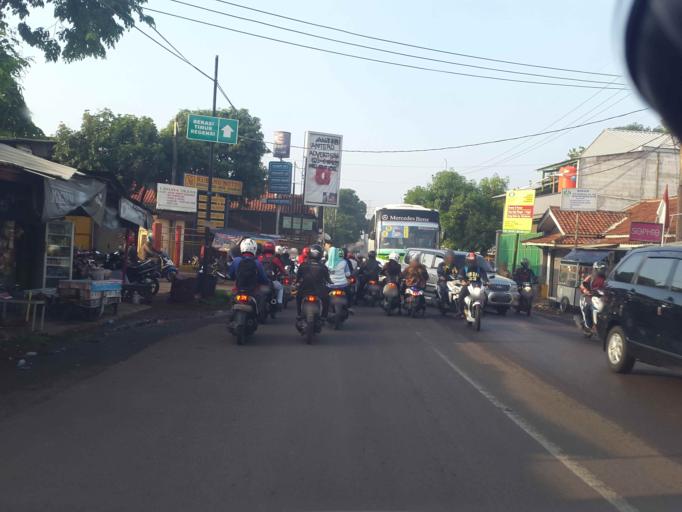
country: ID
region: West Java
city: Cikarang
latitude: -6.2837
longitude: 107.0721
